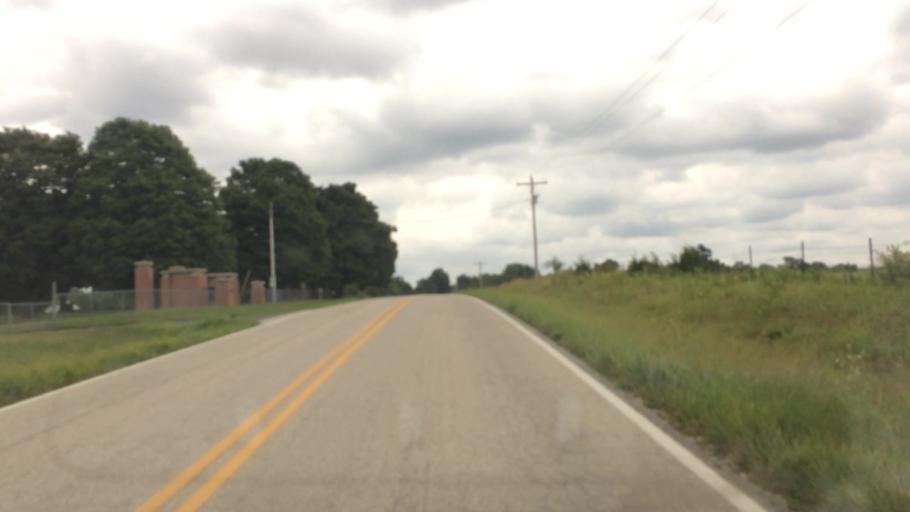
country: US
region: Missouri
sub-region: Greene County
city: Strafford
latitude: 37.2998
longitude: -93.1275
